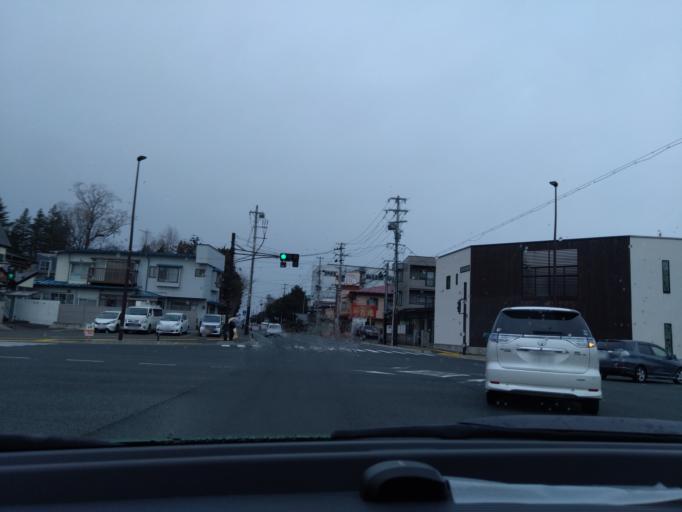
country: JP
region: Iwate
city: Morioka-shi
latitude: 39.7116
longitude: 141.1418
